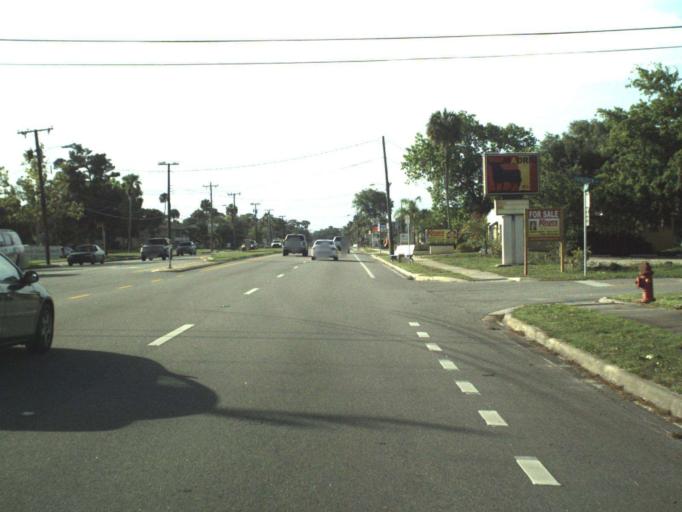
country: US
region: Florida
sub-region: Volusia County
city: Edgewater
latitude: 28.9963
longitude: -80.9100
